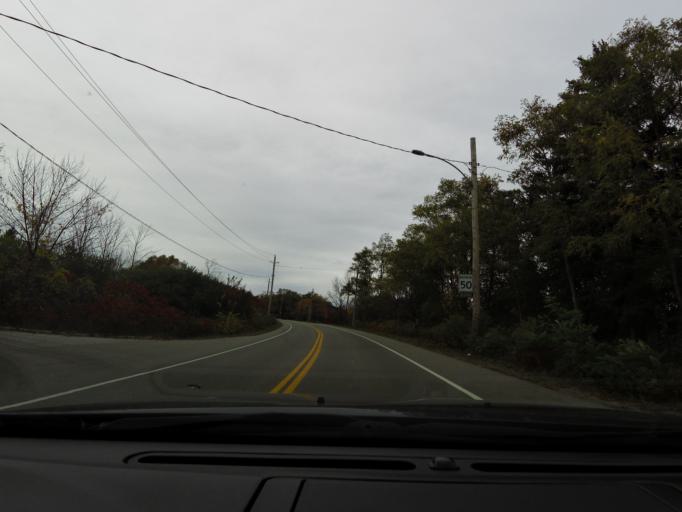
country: CA
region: Ontario
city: Hamilton
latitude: 43.2981
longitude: -79.8841
